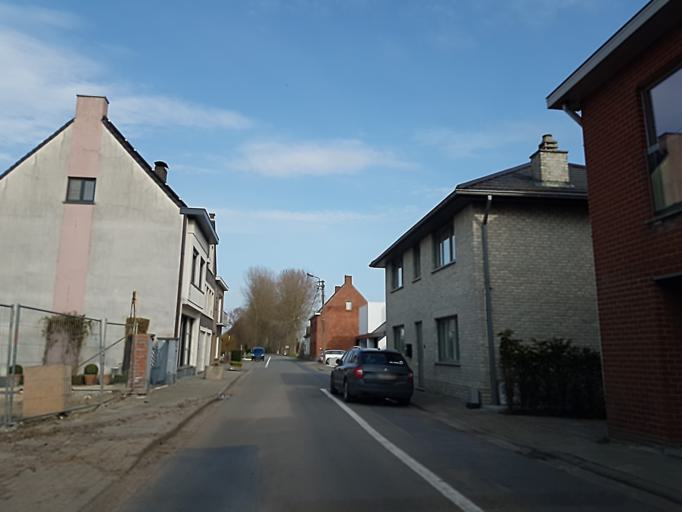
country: BE
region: Flanders
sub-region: Provincie Oost-Vlaanderen
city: Kaprijke
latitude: 51.2766
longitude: 3.6303
